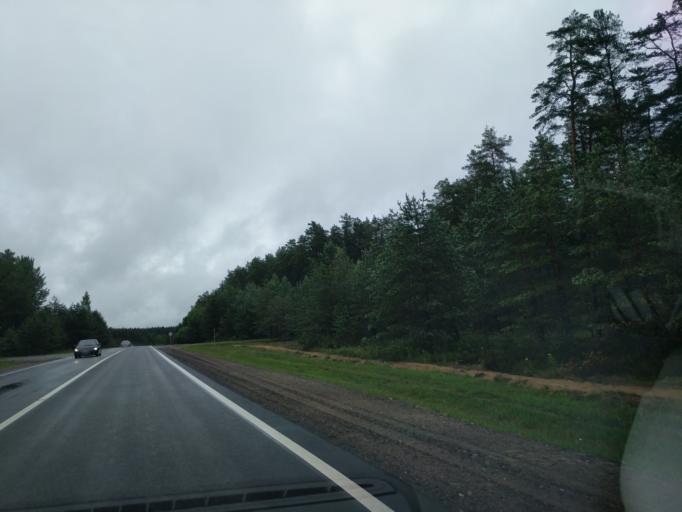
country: BY
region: Minsk
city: Syomkava
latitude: 54.2013
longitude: 27.4950
